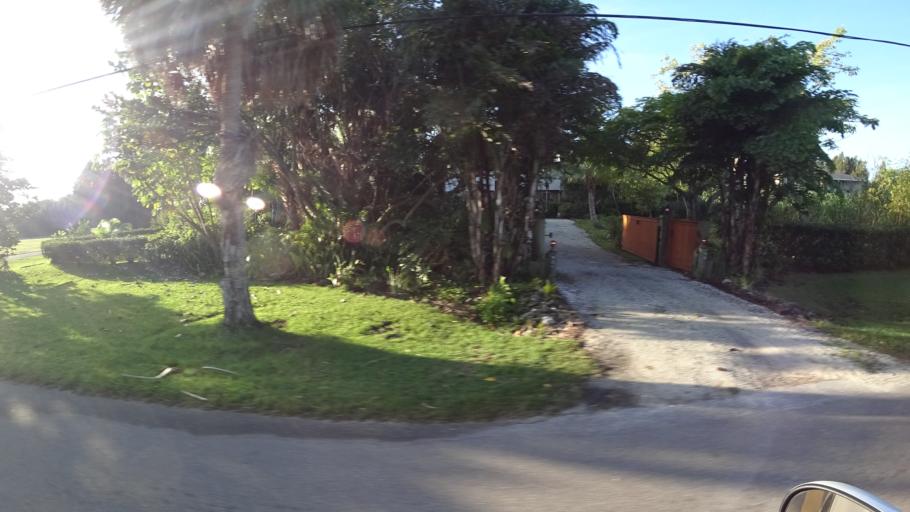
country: US
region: Florida
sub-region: Manatee County
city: Memphis
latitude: 27.5649
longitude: -82.5894
